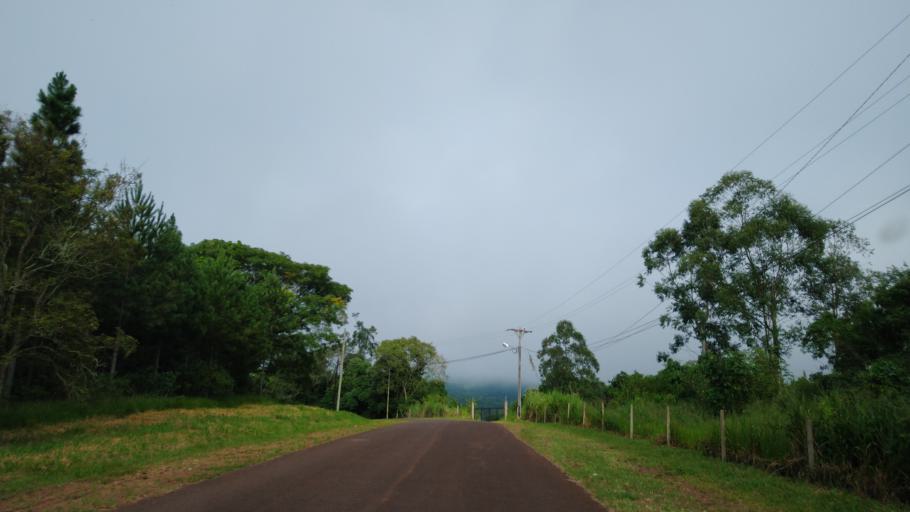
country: AR
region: Misiones
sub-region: Departamento de Montecarlo
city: Montecarlo
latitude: -26.5675
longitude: -54.7962
